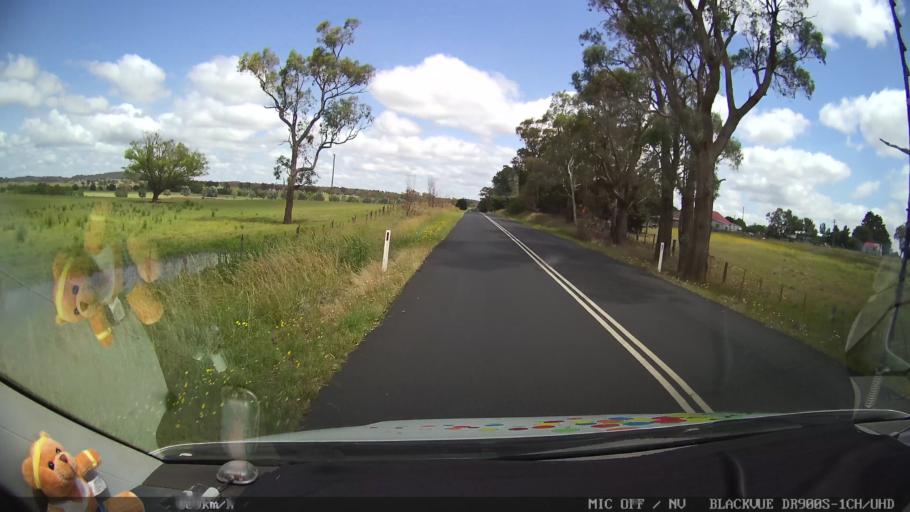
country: AU
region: New South Wales
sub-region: Glen Innes Severn
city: Glen Innes
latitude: -29.6461
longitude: 151.6914
